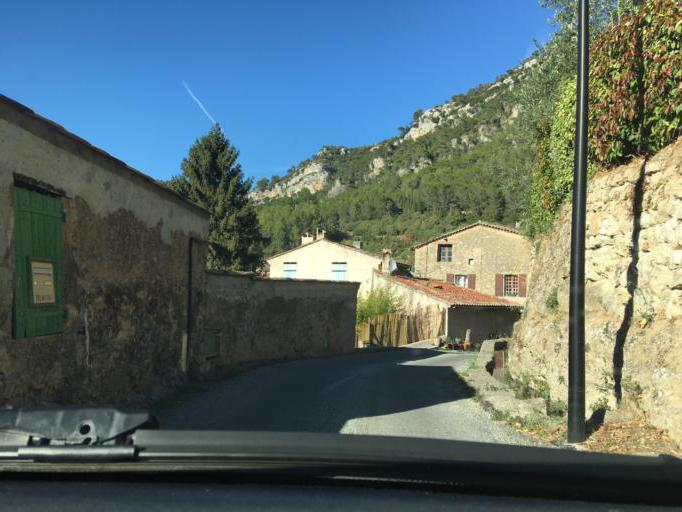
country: FR
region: Provence-Alpes-Cote d'Azur
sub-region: Departement du Var
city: Flayosc
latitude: 43.5756
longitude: 6.4244
